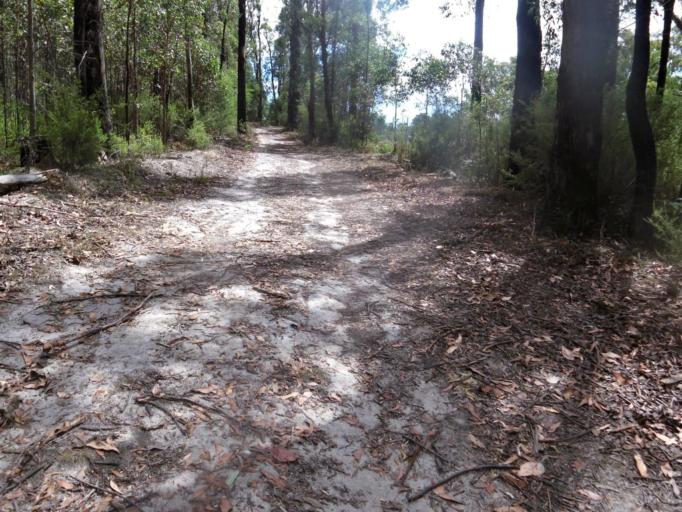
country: AU
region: Victoria
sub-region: Nillumbik
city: Saint Andrews
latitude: -37.5438
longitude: 145.3415
